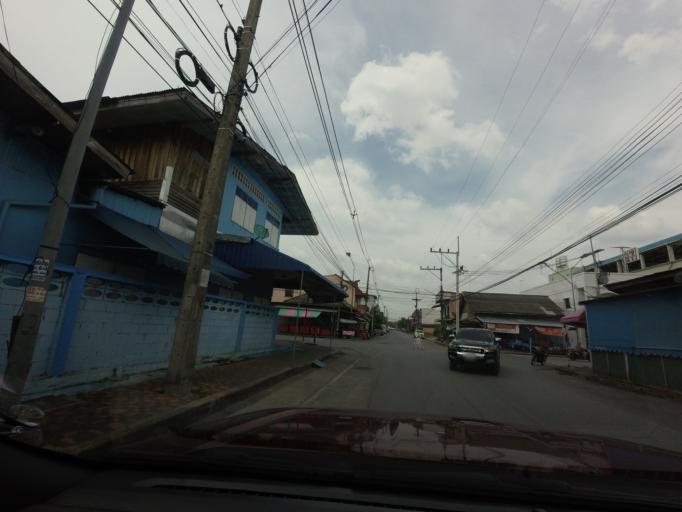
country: TH
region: Yala
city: Yala
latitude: 6.5632
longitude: 101.2948
